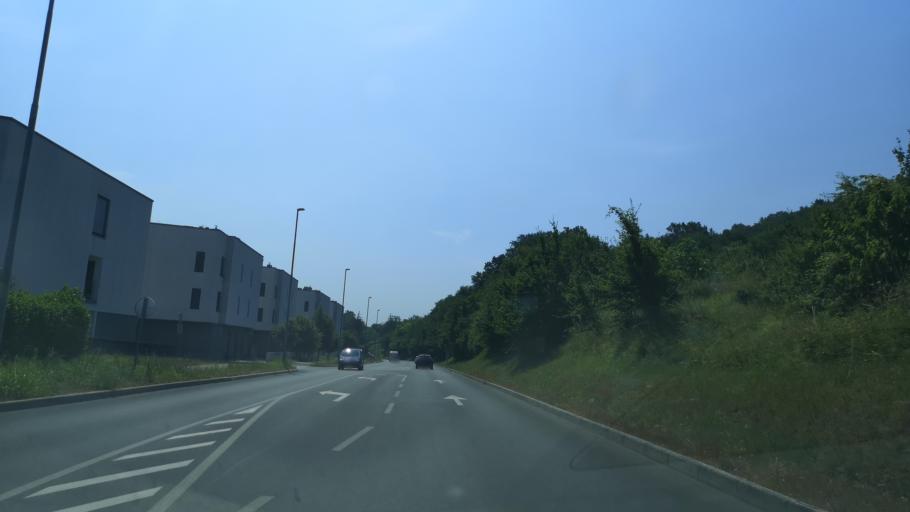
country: SI
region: Koper-Capodistria
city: Koper
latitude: 45.5411
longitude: 13.6990
